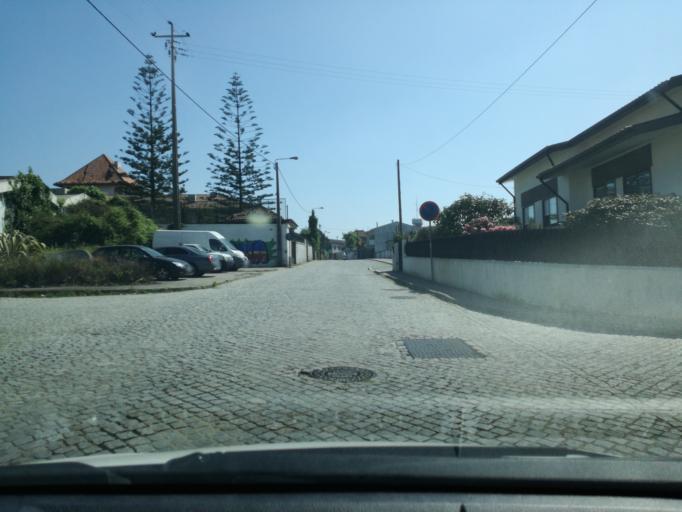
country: PT
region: Porto
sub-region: Maia
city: Gemunde
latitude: 41.2490
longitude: -8.6651
